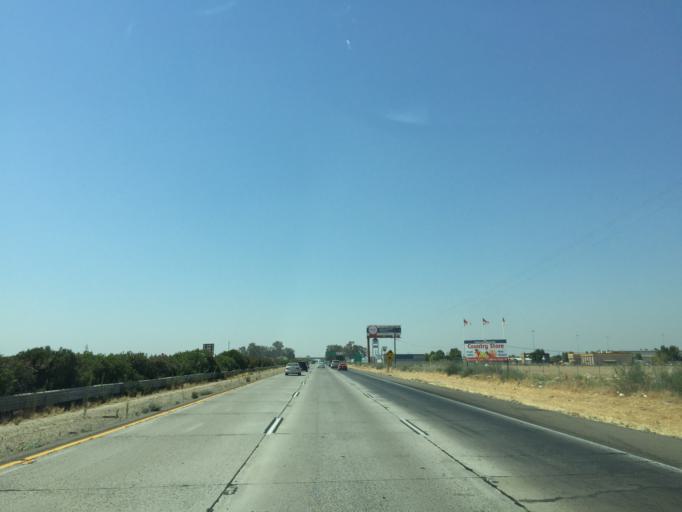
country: US
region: California
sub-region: Fresno County
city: Fowler
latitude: 36.5987
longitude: -119.6536
